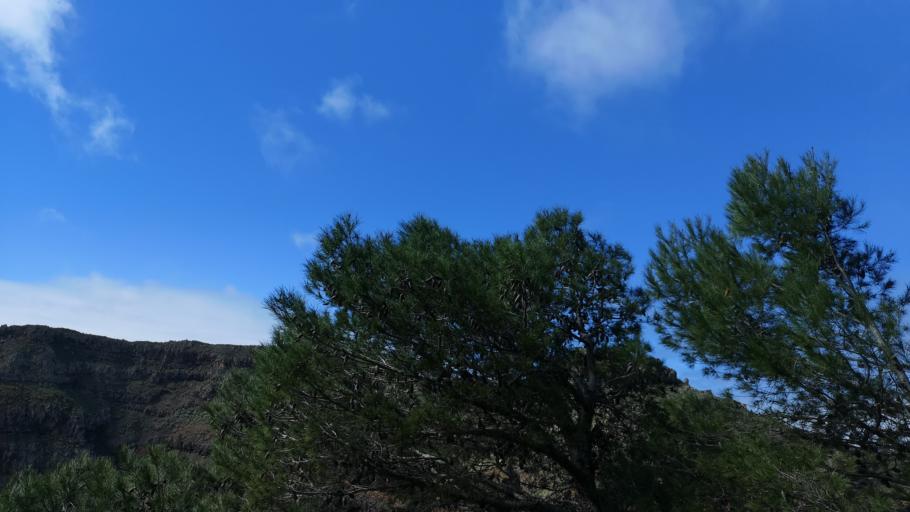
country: ES
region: Canary Islands
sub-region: Provincia de Santa Cruz de Tenerife
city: Vallehermosa
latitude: 28.1280
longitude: -17.3217
